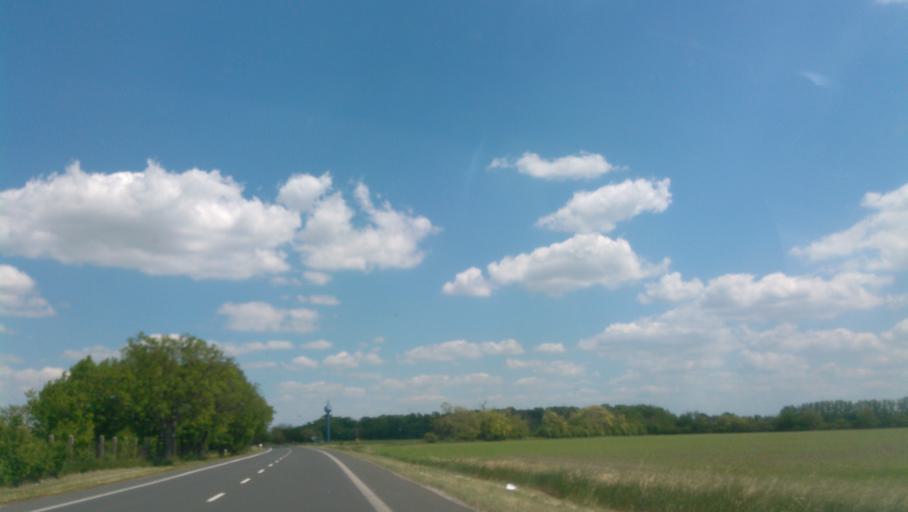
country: SK
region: Trnavsky
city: Samorin
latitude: 48.0027
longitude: 17.3888
